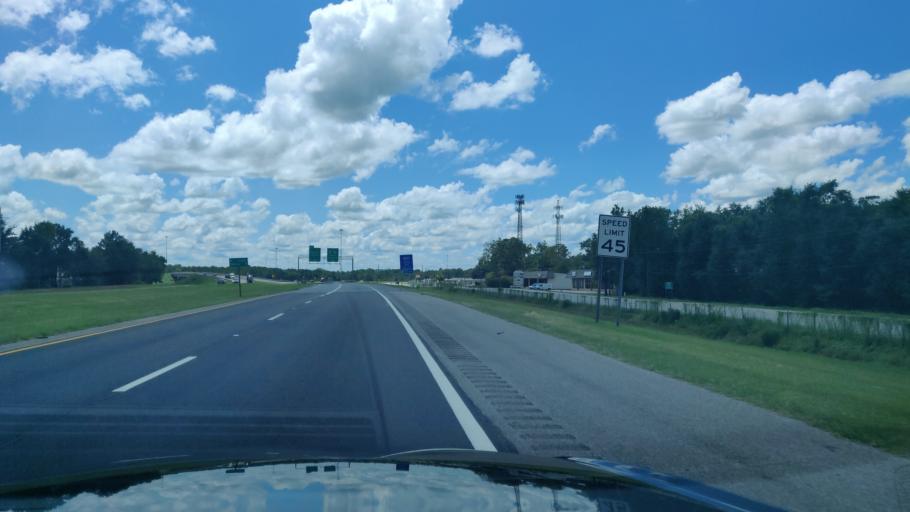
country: US
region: Georgia
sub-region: Dougherty County
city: Albany
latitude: 31.6230
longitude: -84.2241
